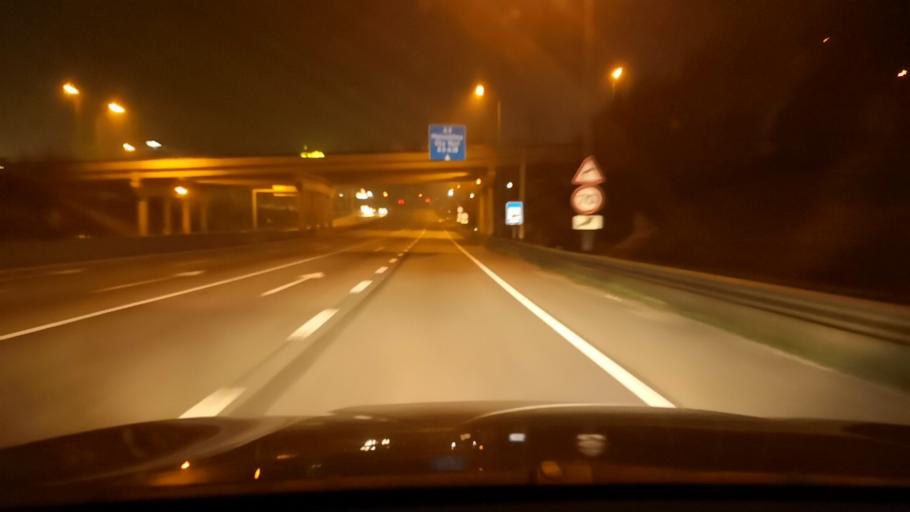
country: PT
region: Porto
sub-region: Maia
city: Leca do Bailio
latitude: 41.2038
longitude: -8.6275
